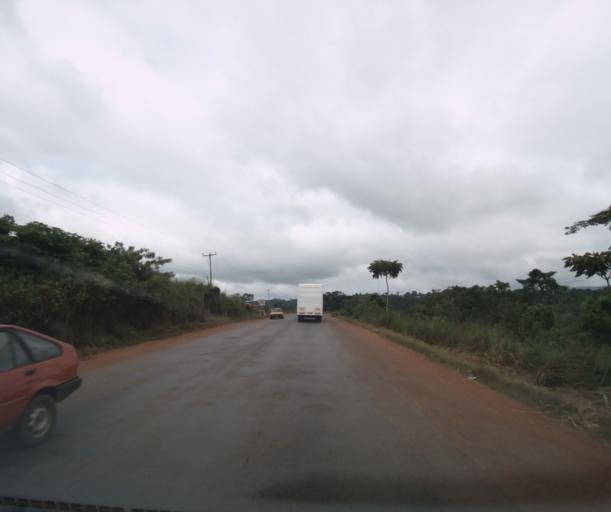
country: CM
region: Centre
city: Mbankomo
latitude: 3.7846
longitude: 11.4603
